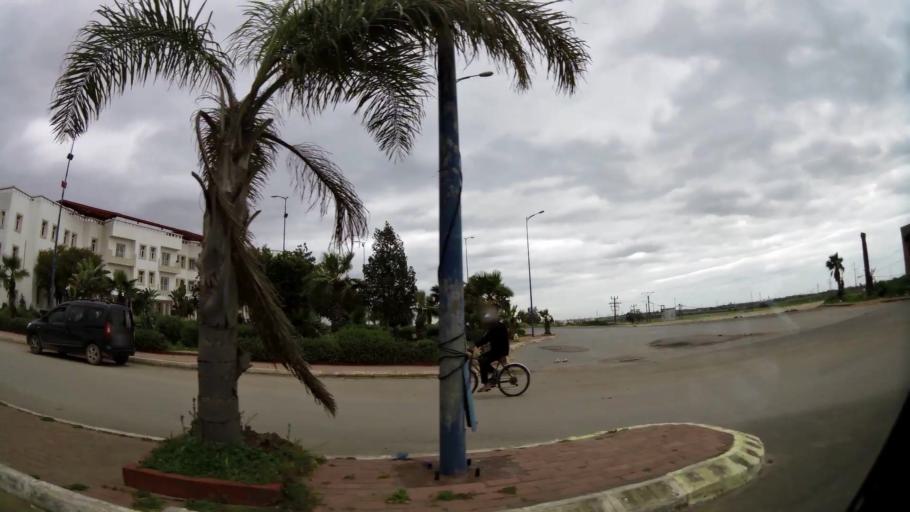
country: MA
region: Grand Casablanca
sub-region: Mediouna
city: Tit Mellil
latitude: 33.5516
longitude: -7.5316
